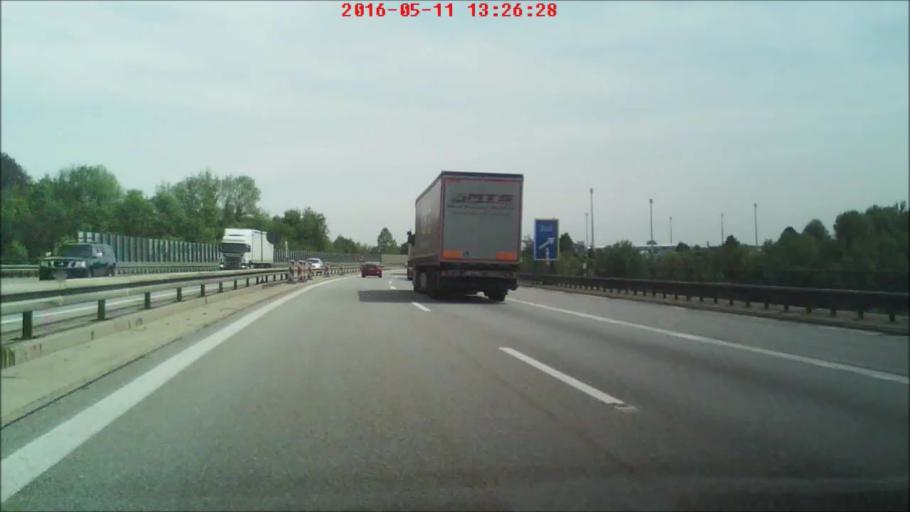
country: AT
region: Upper Austria
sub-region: Politischer Bezirk Scharding
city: Sankt Florian am Inn
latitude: 48.4118
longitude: 13.4249
